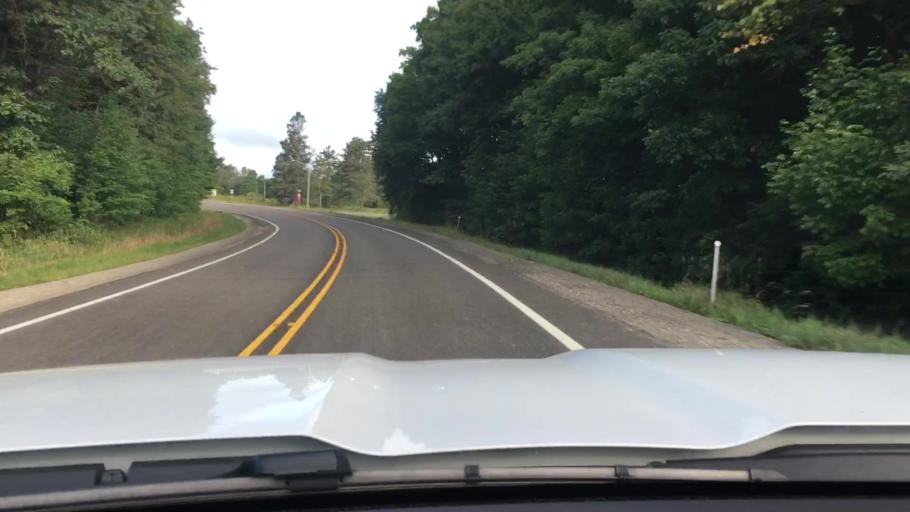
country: US
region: Michigan
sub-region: Lapeer County
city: Barnes Lake-Millers Lake
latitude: 43.3362
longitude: -83.3249
